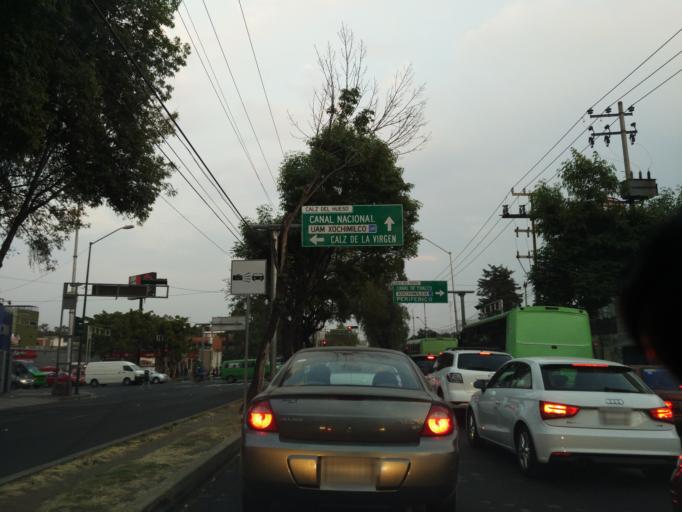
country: MX
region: Mexico City
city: Xochimilco
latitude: 19.3008
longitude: -99.1142
